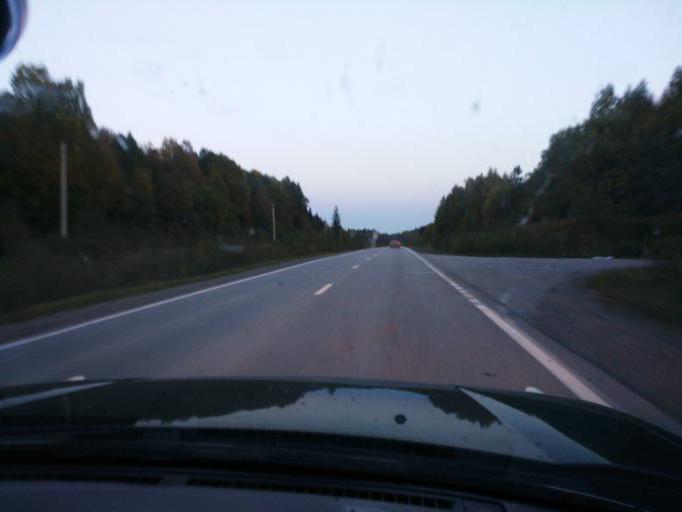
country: RU
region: Perm
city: Verkhnechusovskiye Gorodki
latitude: 58.2543
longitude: 57.0038
